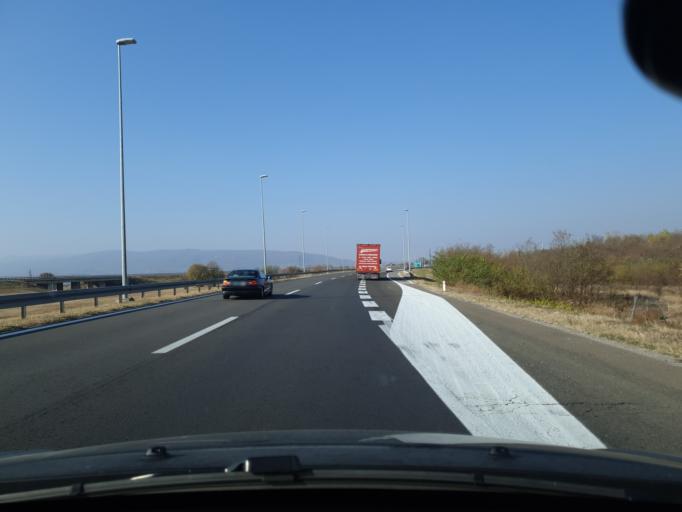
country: RS
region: Central Serbia
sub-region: Nisavski Okrug
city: Nis
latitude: 43.3566
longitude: 21.8281
